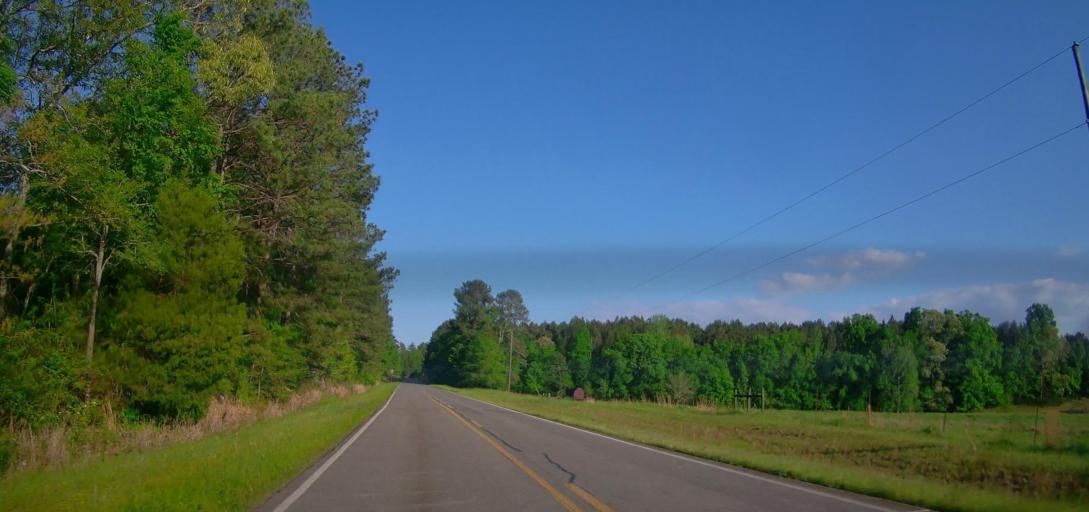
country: US
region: Georgia
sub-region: Putnam County
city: Eatonton
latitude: 33.2896
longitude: -83.3297
